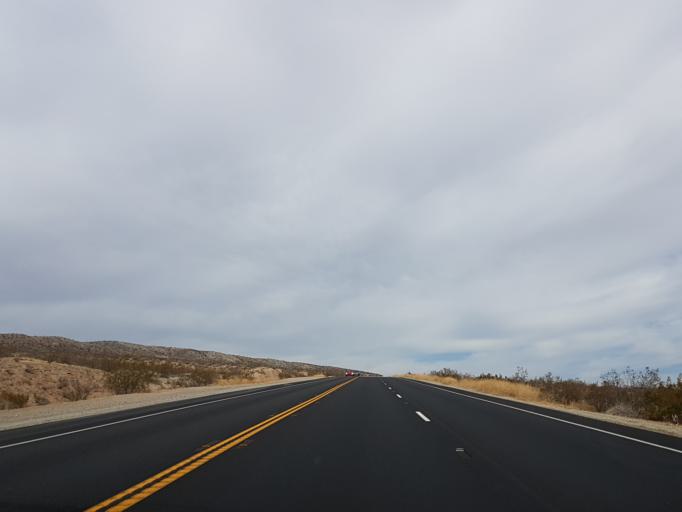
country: US
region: California
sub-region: Kern County
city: Ridgecrest
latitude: 35.4420
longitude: -117.6652
